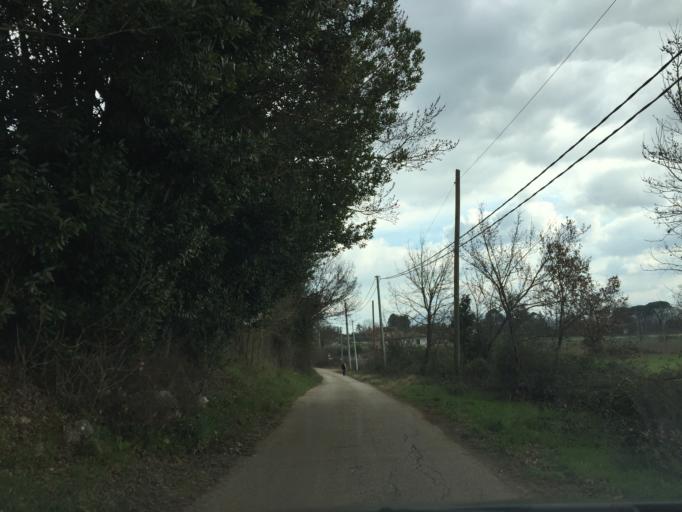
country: IT
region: Latium
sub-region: Provincia di Frosinone
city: Villa Santa Lucia
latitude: 41.4884
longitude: 13.7886
